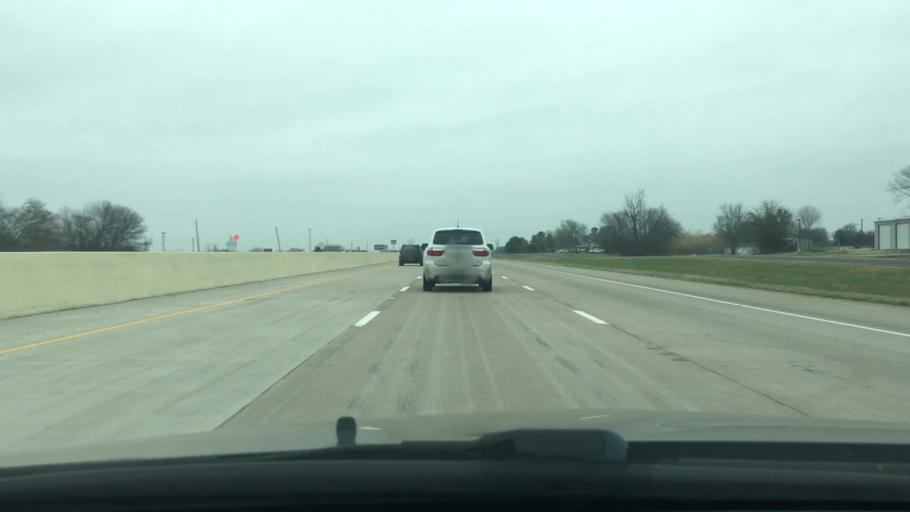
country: US
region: Texas
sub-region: Navarro County
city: Corsicana
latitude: 32.0182
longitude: -96.4381
